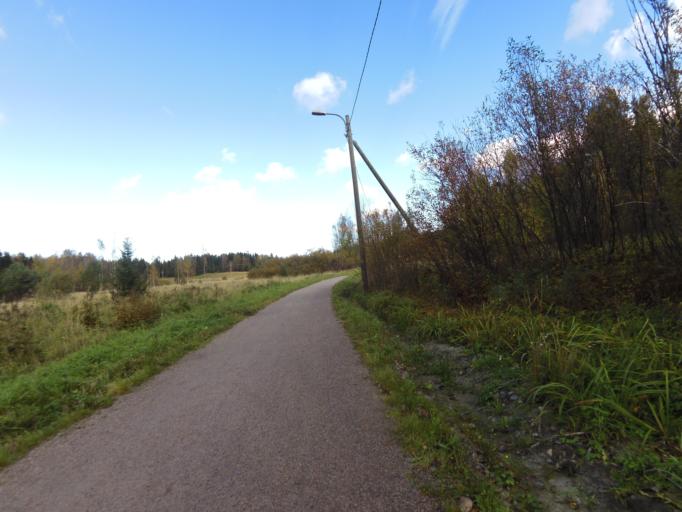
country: FI
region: Uusimaa
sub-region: Helsinki
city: Espoo
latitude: 60.1846
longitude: 24.6636
